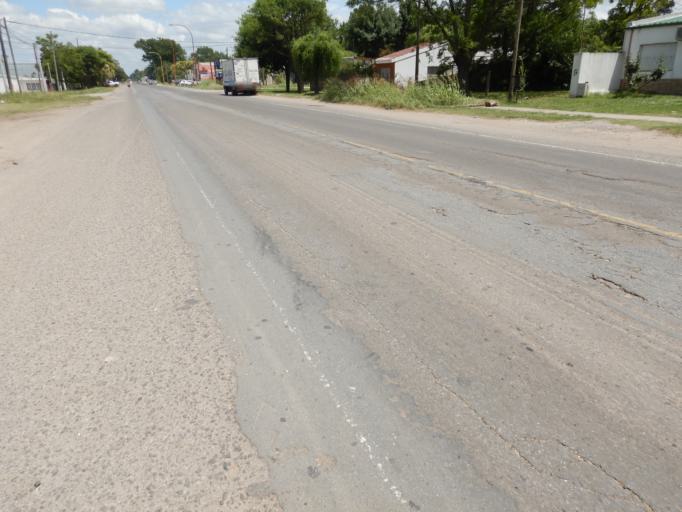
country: AR
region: Santa Fe
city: Canada de Gomez
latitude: -32.8073
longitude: -61.4121
